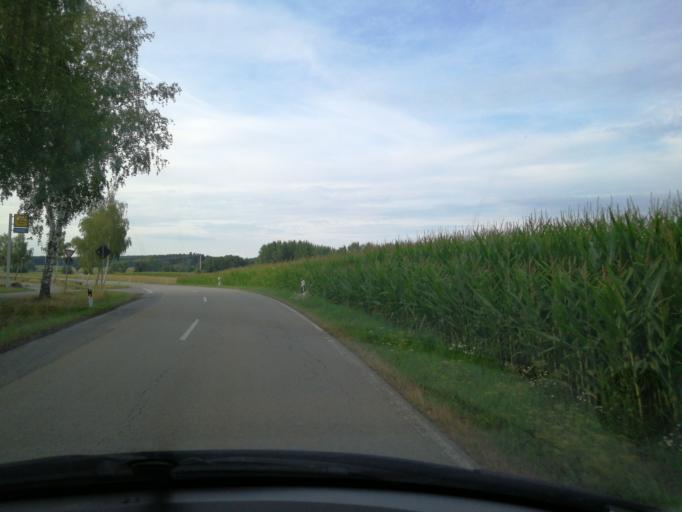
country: DE
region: Bavaria
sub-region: Lower Bavaria
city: Wiesenfelden
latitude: 49.0447
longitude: 12.5332
